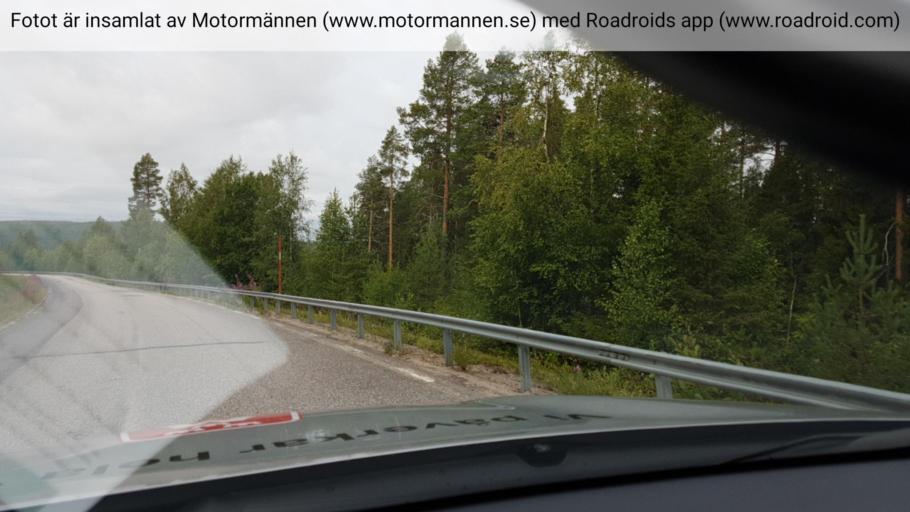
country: SE
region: Norrbotten
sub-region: Bodens Kommun
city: Saevast
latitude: 65.6714
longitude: 21.6987
